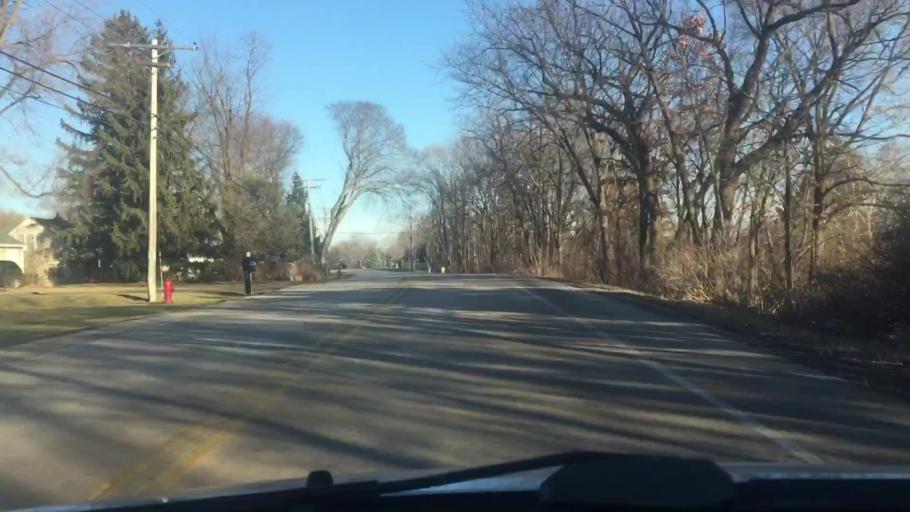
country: US
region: Wisconsin
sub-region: Waukesha County
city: Brookfield
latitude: 43.0591
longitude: -88.1777
